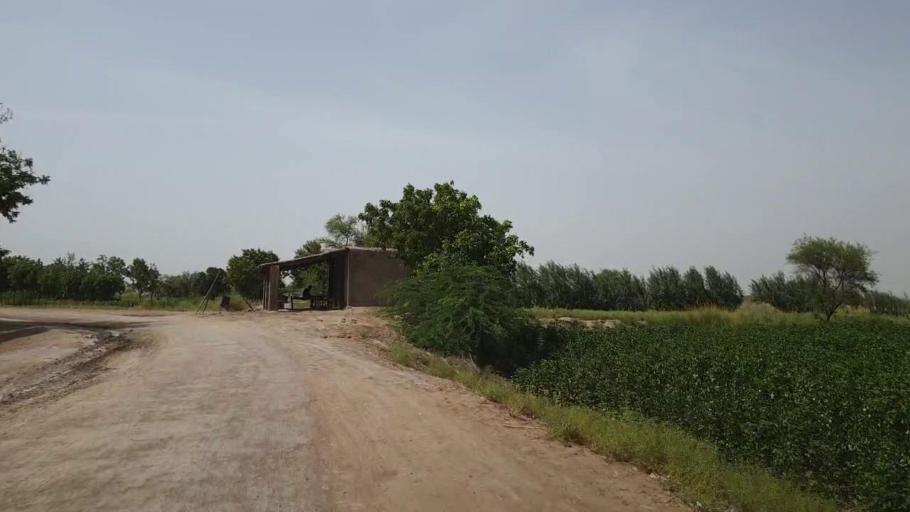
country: PK
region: Sindh
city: Bandhi
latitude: 26.5380
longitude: 68.4077
